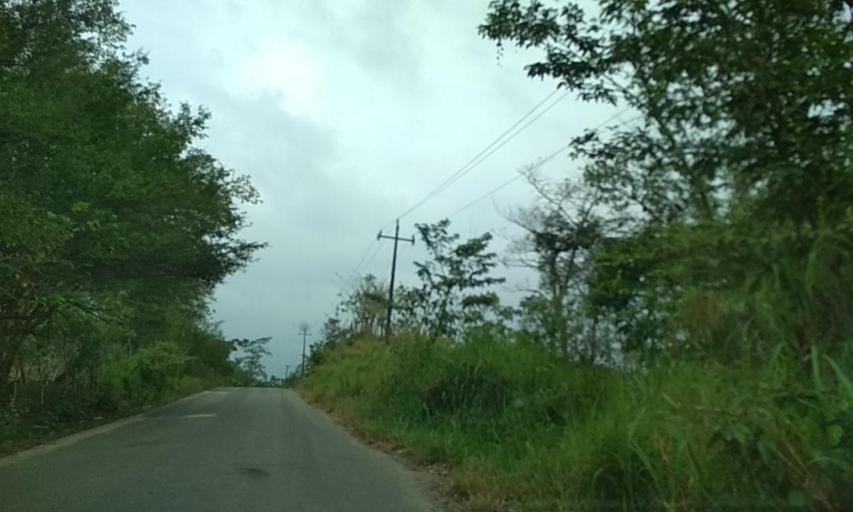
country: MX
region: Tabasco
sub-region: Huimanguillo
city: Francisco Rueda
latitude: 17.6028
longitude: -94.0919
